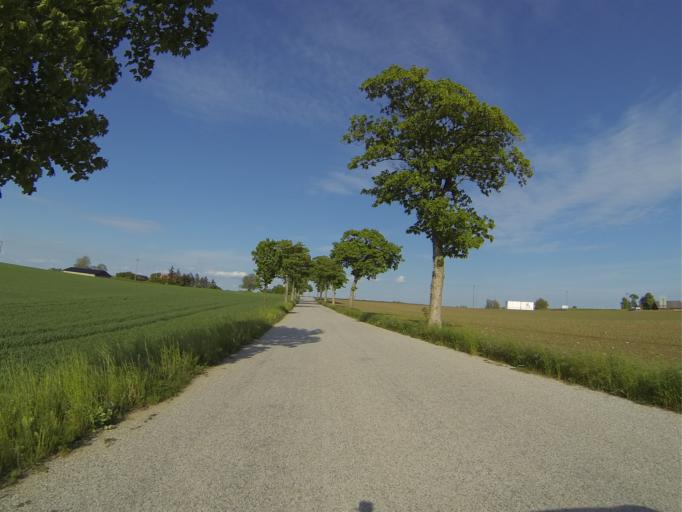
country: SE
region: Skane
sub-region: Staffanstorps Kommun
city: Hjaerup
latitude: 55.6194
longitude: 13.1373
